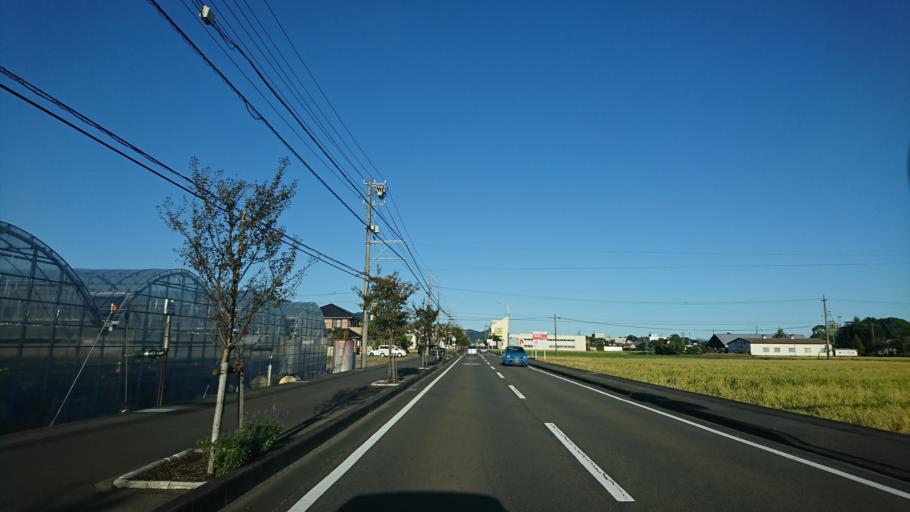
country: JP
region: Shizuoka
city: Fujieda
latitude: 34.8653
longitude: 138.2674
